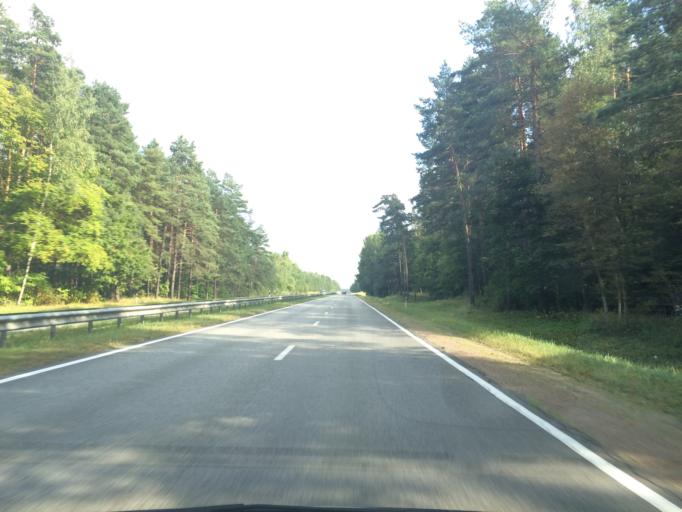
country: LV
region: Ikskile
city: Ikskile
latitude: 56.8314
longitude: 24.5114
